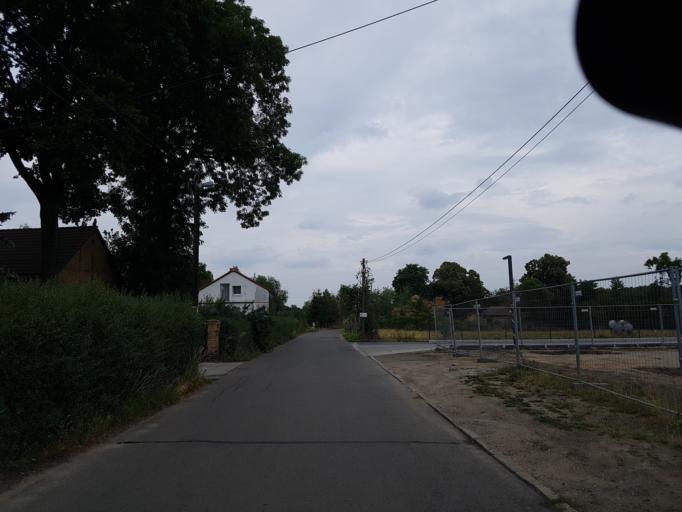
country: DE
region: Brandenburg
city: Schipkau
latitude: 51.5556
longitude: 13.8855
